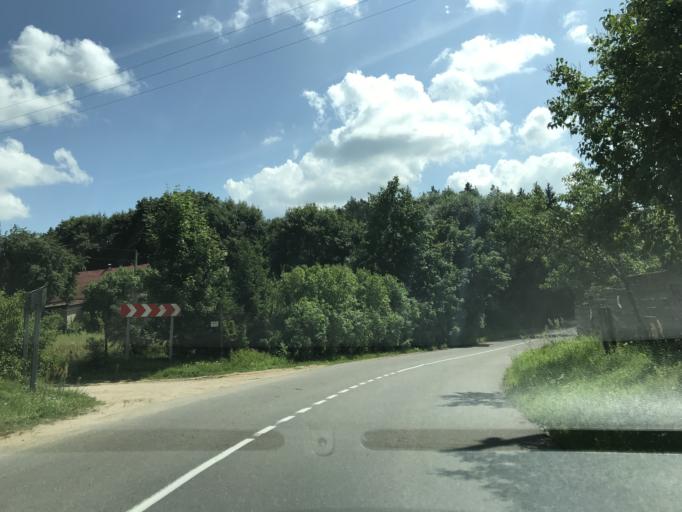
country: BY
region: Minsk
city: Rakaw
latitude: 53.9956
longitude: 26.9896
